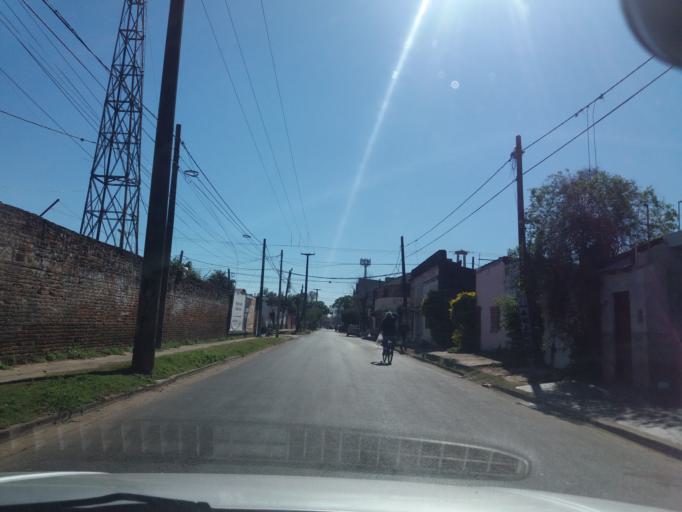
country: AR
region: Corrientes
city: Corrientes
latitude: -27.4826
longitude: -58.8441
